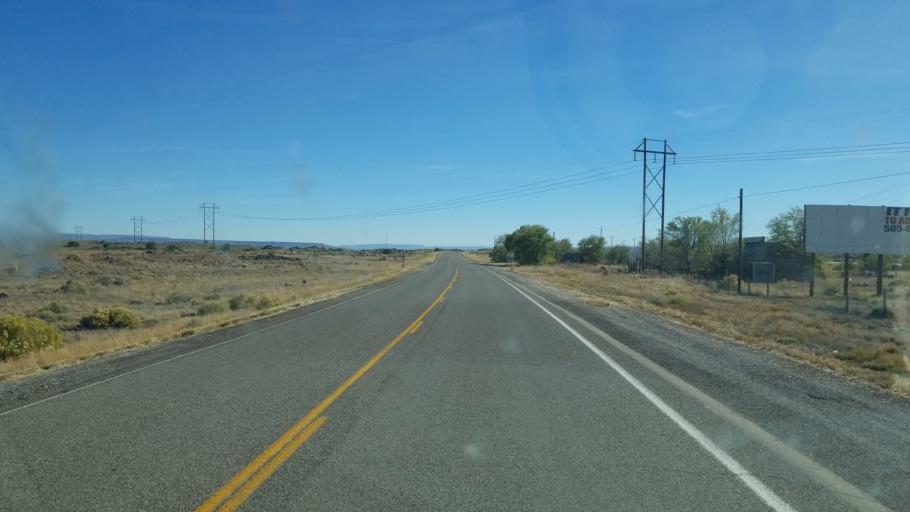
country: US
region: New Mexico
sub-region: Cibola County
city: Milan
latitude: 35.3132
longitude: -107.9909
